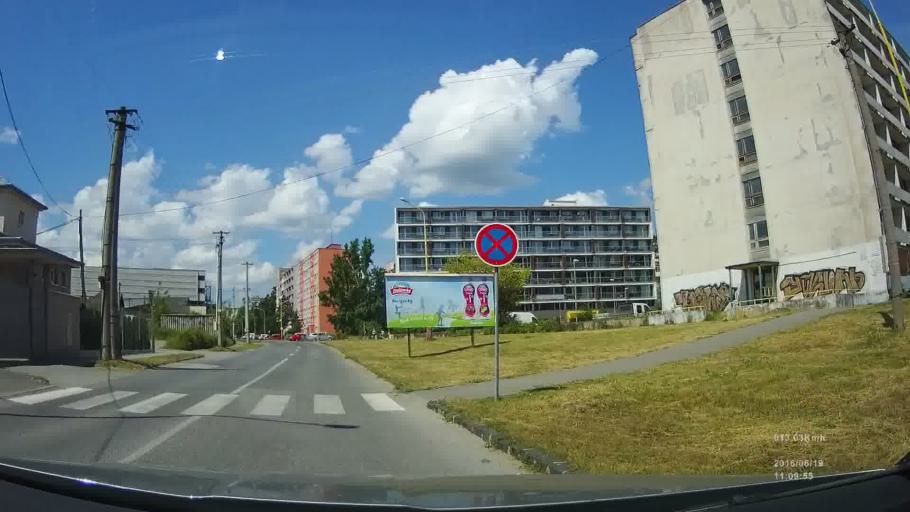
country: SK
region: Kosicky
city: Kosice
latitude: 48.7161
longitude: 21.2406
